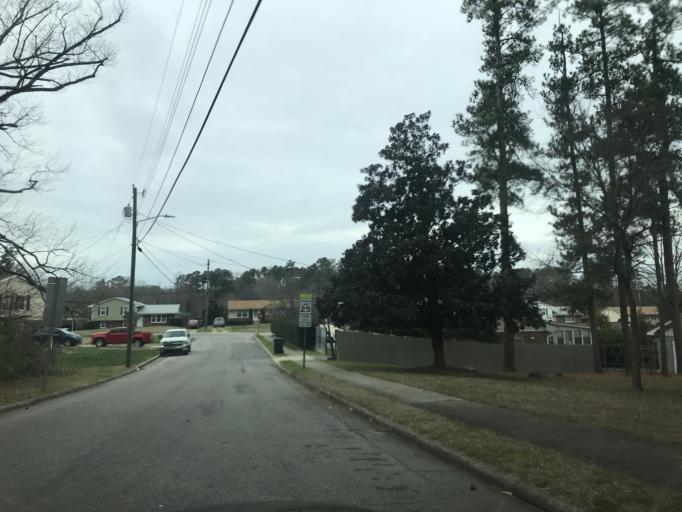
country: US
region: North Carolina
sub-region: Wake County
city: Raleigh
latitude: 35.7966
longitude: -78.6030
